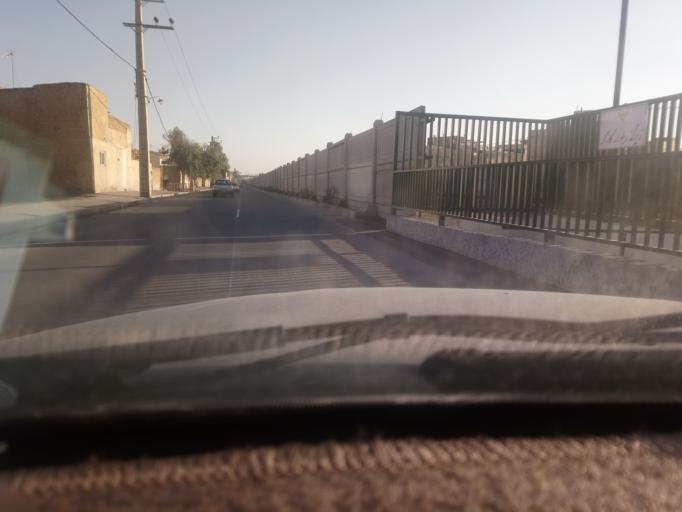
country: IR
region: Qom
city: Qom
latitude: 34.6660
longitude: 50.8668
